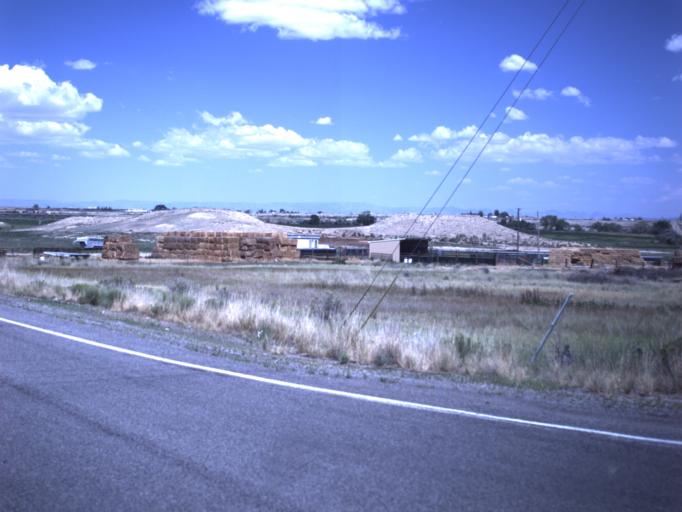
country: US
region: Utah
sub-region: Emery County
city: Huntington
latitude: 39.3451
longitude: -110.9386
